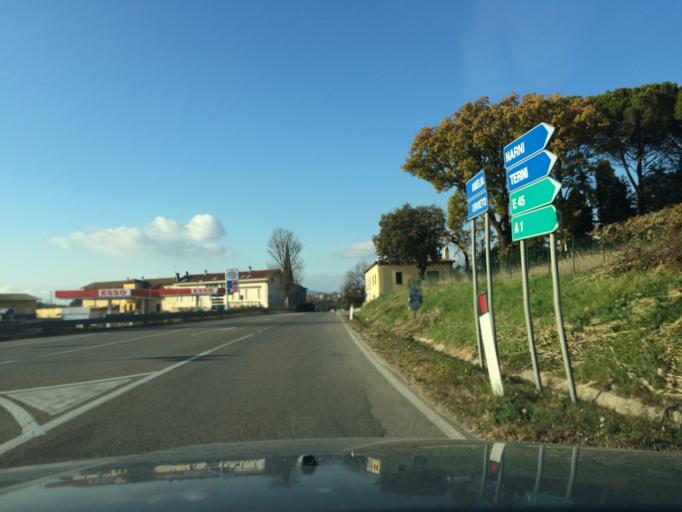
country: IT
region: Umbria
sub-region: Provincia di Terni
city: Fornole
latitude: 42.5457
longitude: 12.4506
